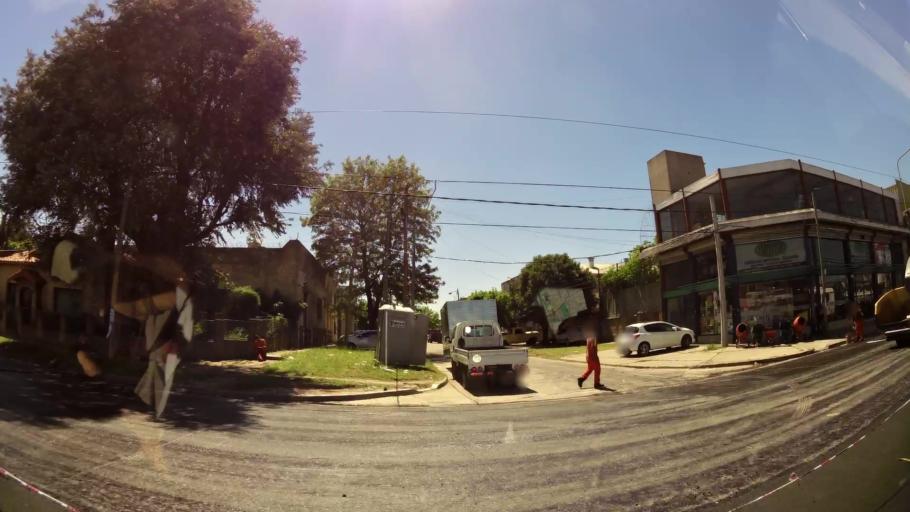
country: AR
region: Buenos Aires
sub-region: Partido de Quilmes
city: Quilmes
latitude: -34.7280
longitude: -58.2840
